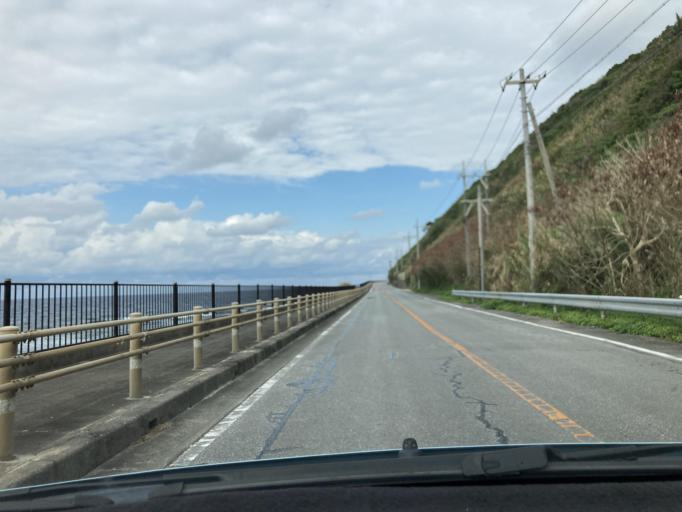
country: JP
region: Okinawa
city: Nago
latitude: 26.7928
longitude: 128.2250
